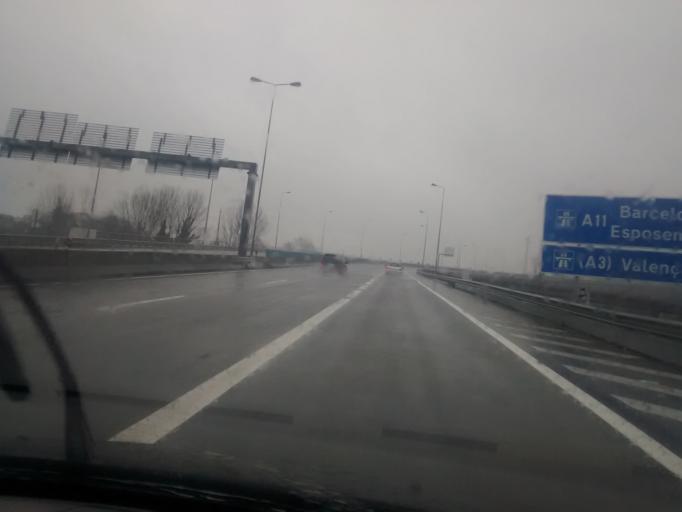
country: PT
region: Braga
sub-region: Braga
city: Braga
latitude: 41.5331
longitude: -8.4452
